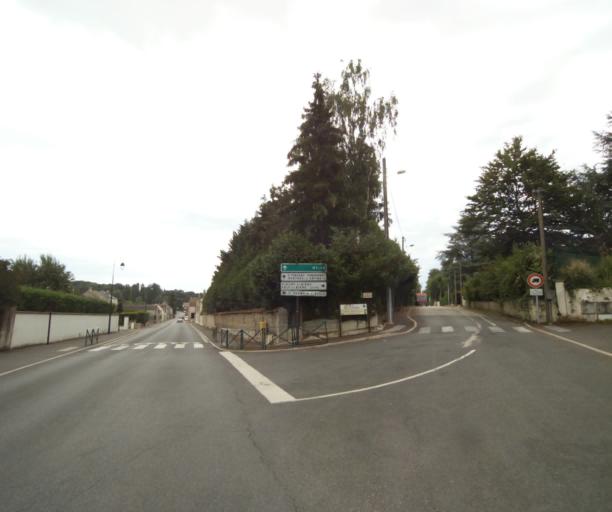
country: FR
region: Ile-de-France
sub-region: Departement de Seine-et-Marne
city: Cely
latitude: 48.4587
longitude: 2.5244
